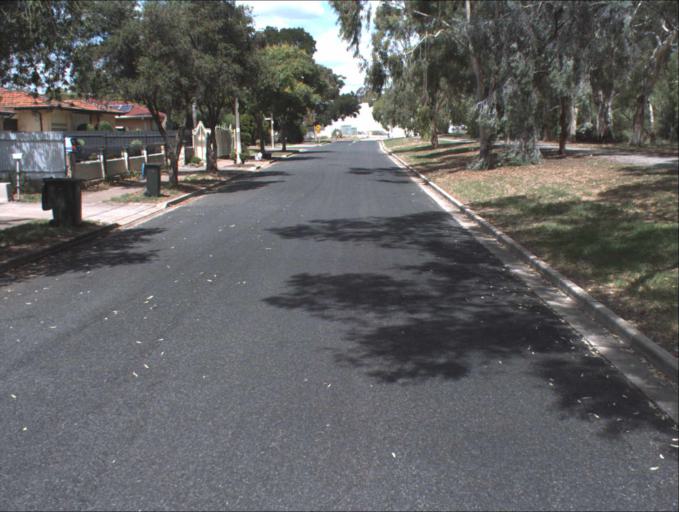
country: AU
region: South Australia
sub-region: Port Adelaide Enfield
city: Gilles Plains
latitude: -34.8436
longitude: 138.6603
